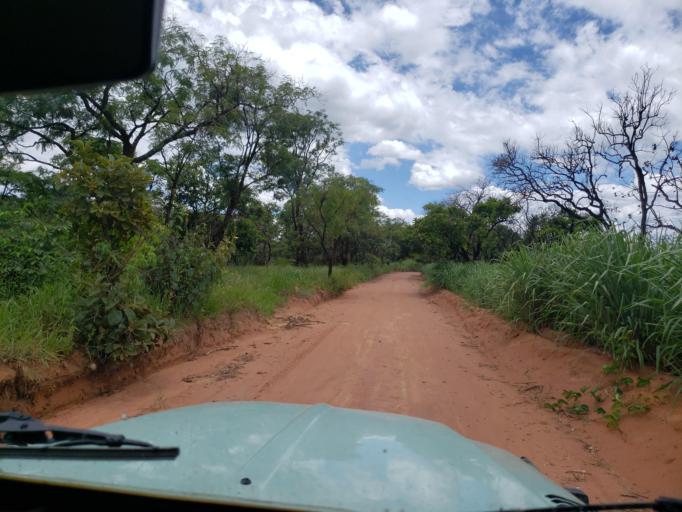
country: BR
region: Sao Paulo
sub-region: Aguai
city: Aguai
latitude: -22.1897
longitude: -46.9499
